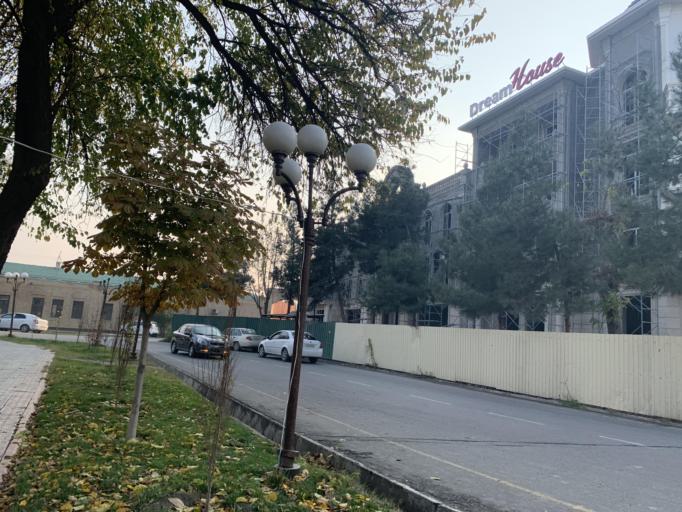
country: UZ
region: Fergana
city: Qo`qon
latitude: 40.5365
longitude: 70.9359
